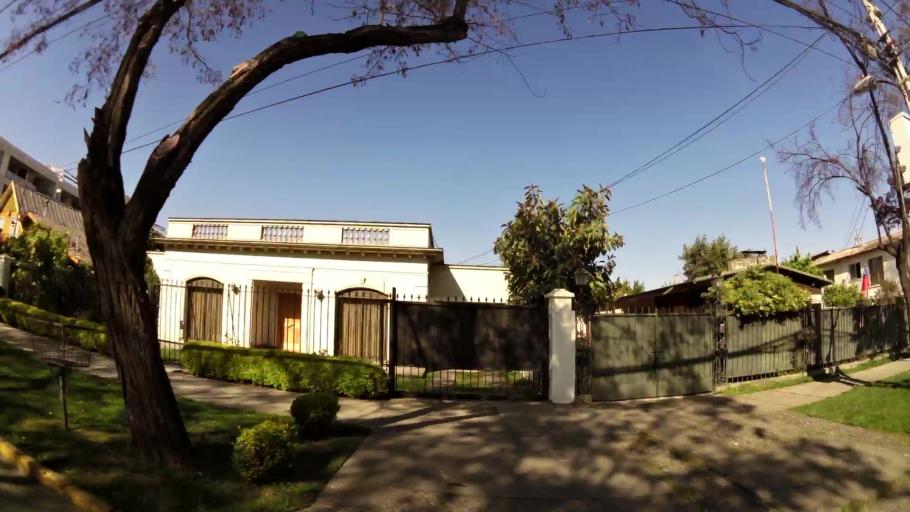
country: CL
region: Santiago Metropolitan
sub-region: Provincia de Santiago
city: Villa Presidente Frei, Nunoa, Santiago, Chile
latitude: -33.4364
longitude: -70.5827
